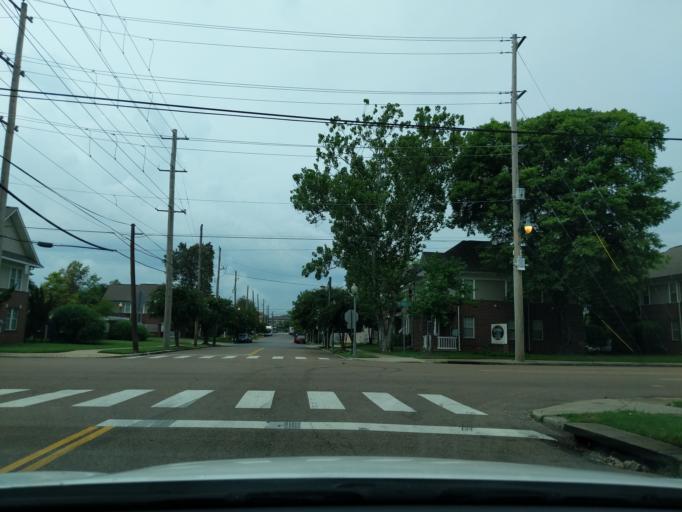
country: US
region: Tennessee
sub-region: Shelby County
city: Memphis
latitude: 35.1584
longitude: -90.0445
